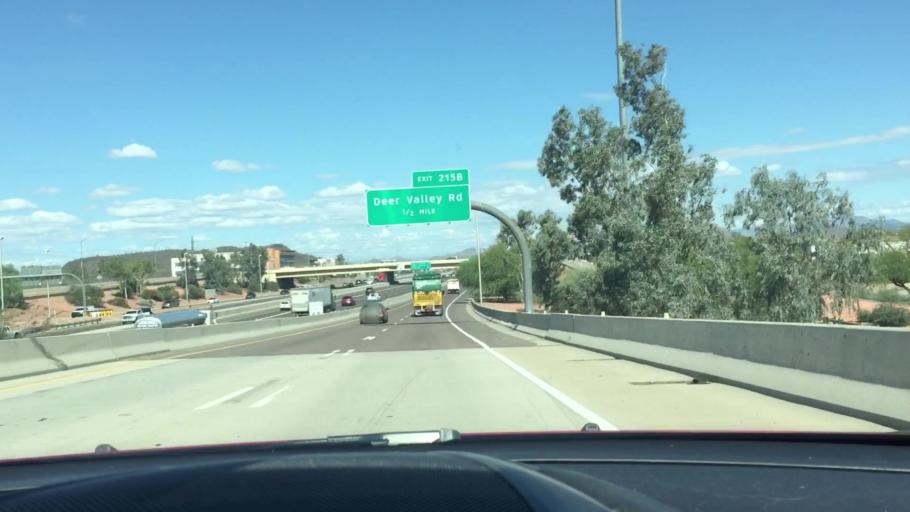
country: US
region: Arizona
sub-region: Maricopa County
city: Glendale
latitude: 33.6735
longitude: -112.1126
